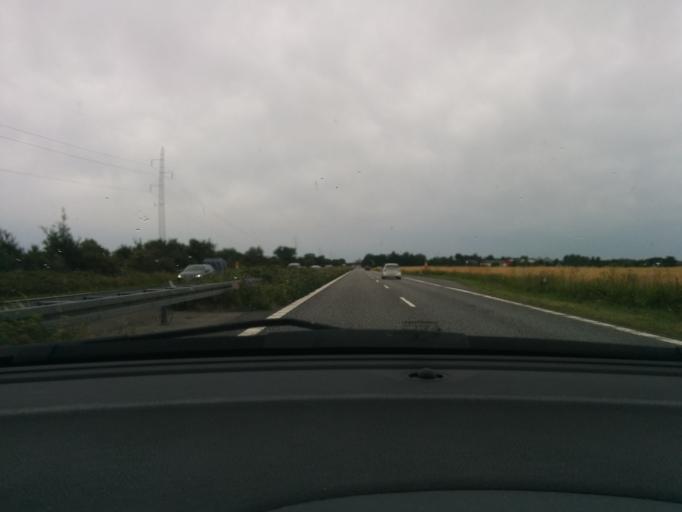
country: DK
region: Zealand
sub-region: Lolland Kommune
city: Rodby
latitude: 54.6767
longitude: 11.3909
